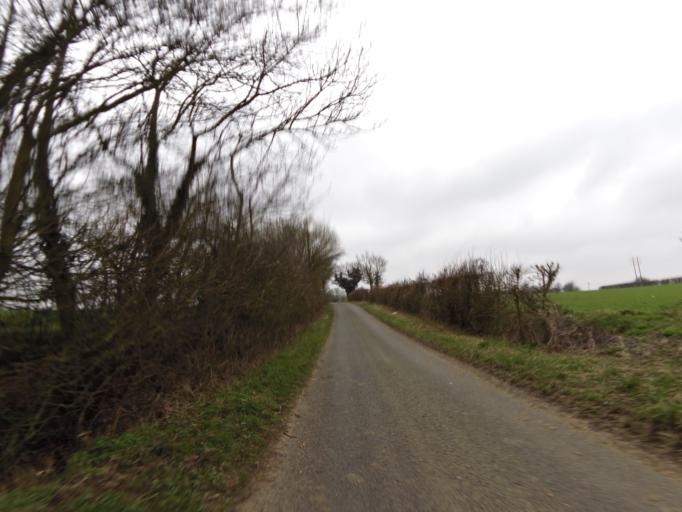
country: GB
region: England
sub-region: Suffolk
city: Framlingham
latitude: 52.2192
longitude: 1.3269
